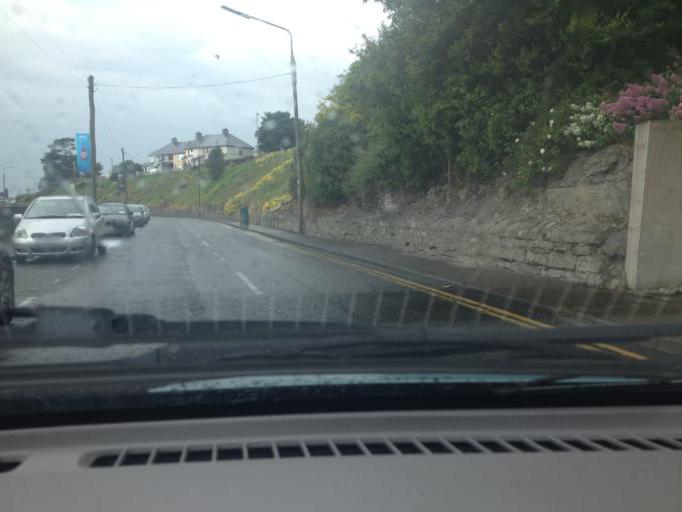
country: IE
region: Connaught
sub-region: Sligo
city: Sligo
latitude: 54.2742
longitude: -8.4742
